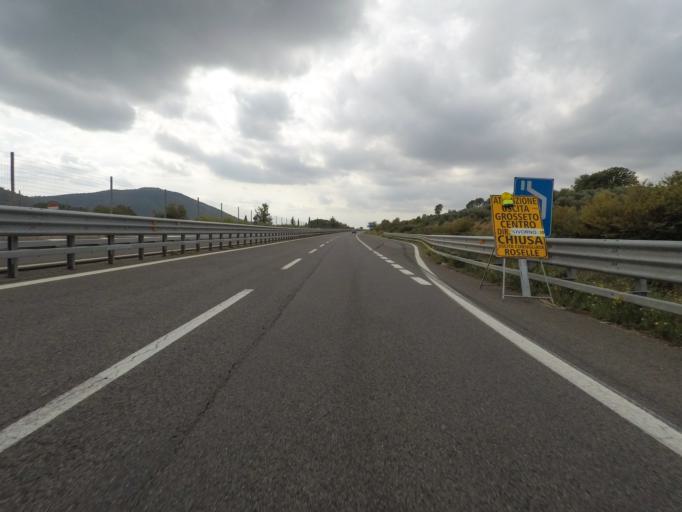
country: IT
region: Tuscany
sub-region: Provincia di Grosseto
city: Bagno Roselle
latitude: 42.8407
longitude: 11.1526
